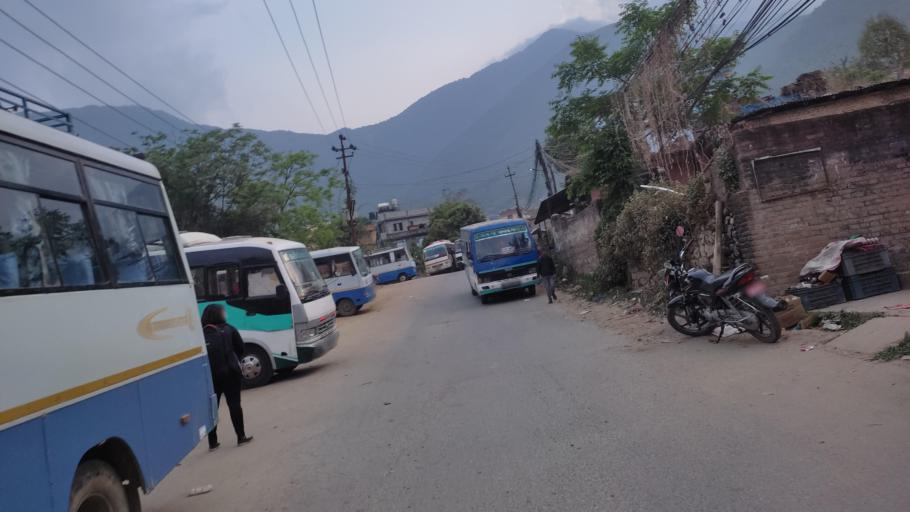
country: NP
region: Central Region
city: Kirtipur
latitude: 27.6652
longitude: 85.2544
